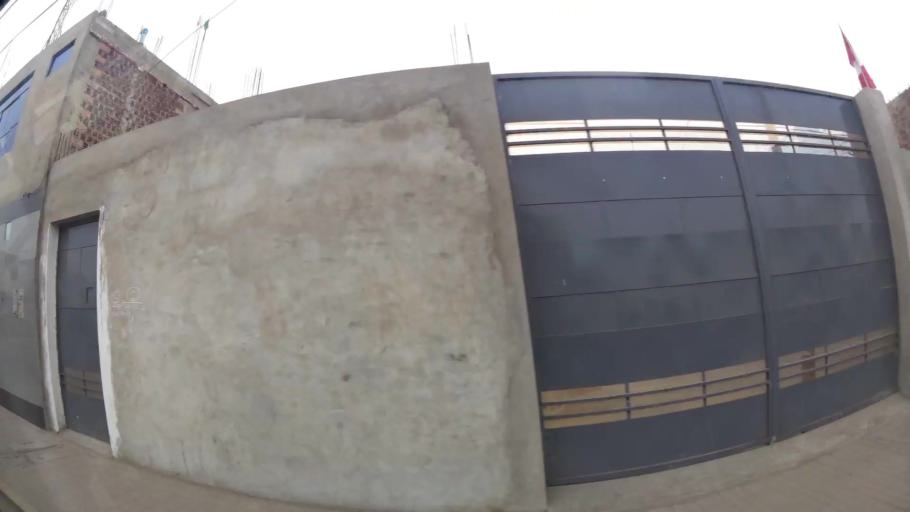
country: PE
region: Ica
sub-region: Provincia de Pisco
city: Pisco
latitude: -13.7107
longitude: -76.2005
